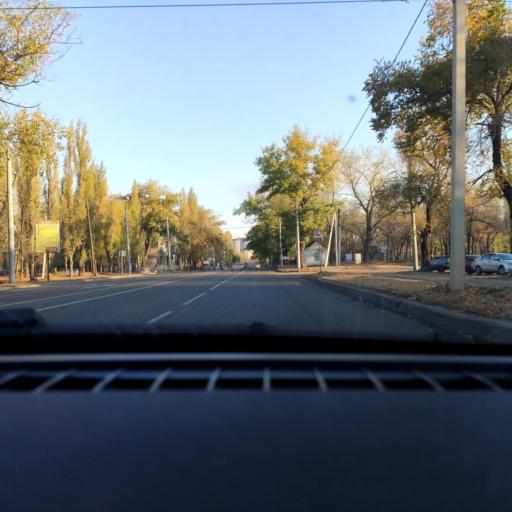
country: RU
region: Voronezj
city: Maslovka
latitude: 51.6087
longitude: 39.2450
